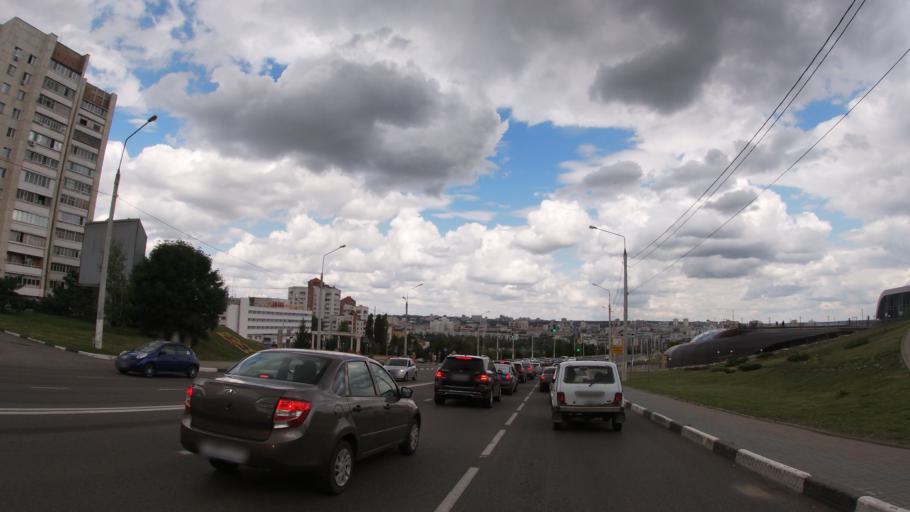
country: RU
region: Belgorod
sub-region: Belgorodskiy Rayon
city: Belgorod
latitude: 50.5802
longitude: 36.5831
